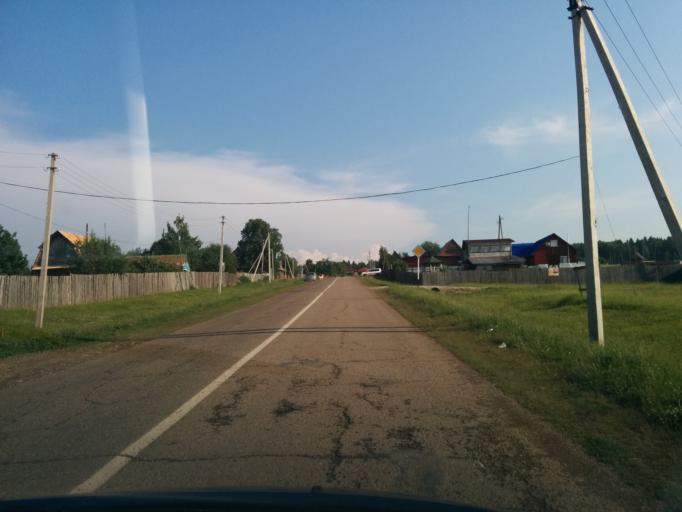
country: RU
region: Perm
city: Polazna
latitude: 58.2491
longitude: 56.2674
